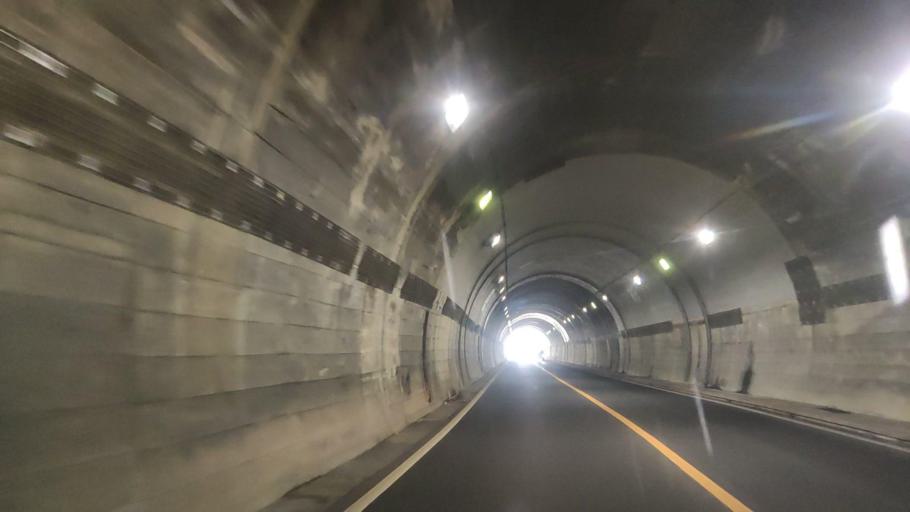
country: JP
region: Tottori
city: Tottori
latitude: 35.5311
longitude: 134.2295
